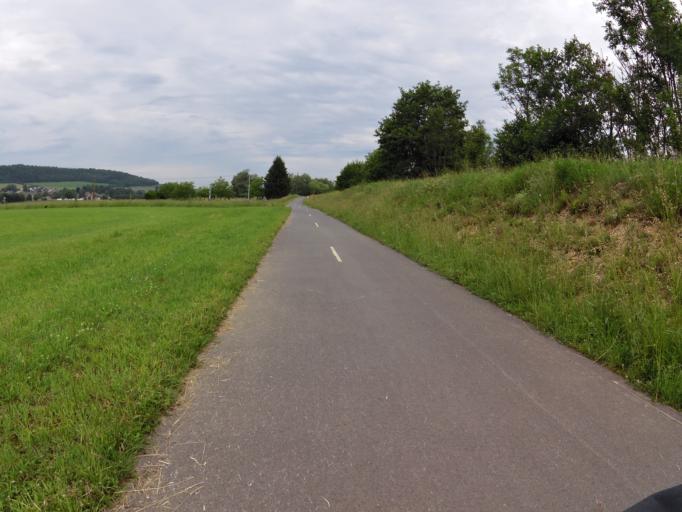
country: FR
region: Champagne-Ardenne
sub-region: Departement des Ardennes
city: Dom-le-Mesnil
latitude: 49.6933
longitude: 4.8183
